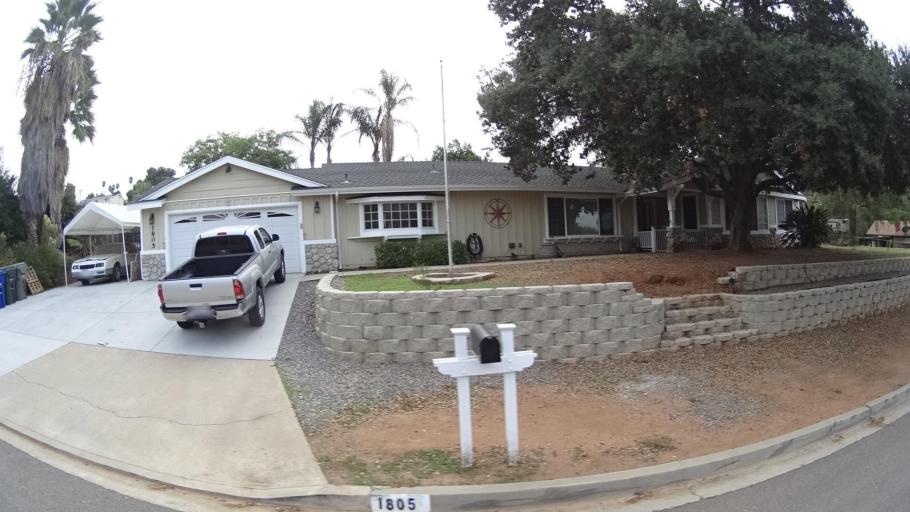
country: US
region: California
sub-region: San Diego County
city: Rancho San Diego
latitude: 32.7583
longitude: -116.9177
